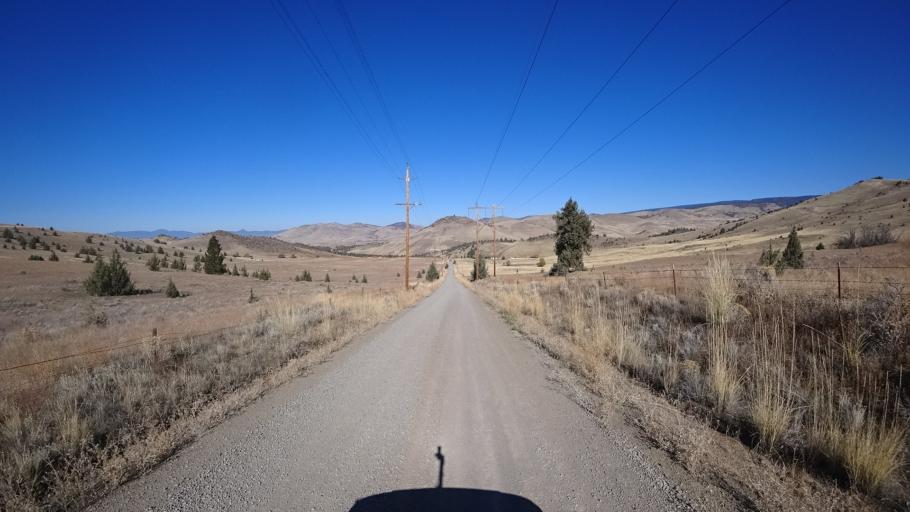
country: US
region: California
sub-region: Siskiyou County
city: Montague
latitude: 41.7772
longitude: -122.3591
